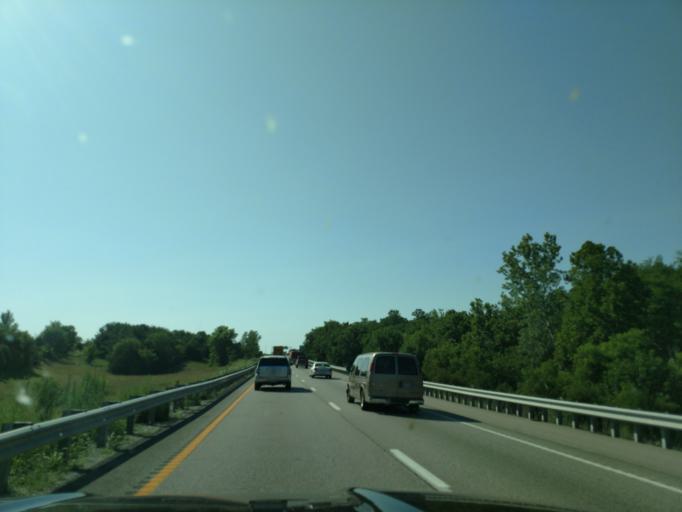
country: US
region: Missouri
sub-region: Andrew County
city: Country Club Village
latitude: 39.8821
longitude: -94.8495
